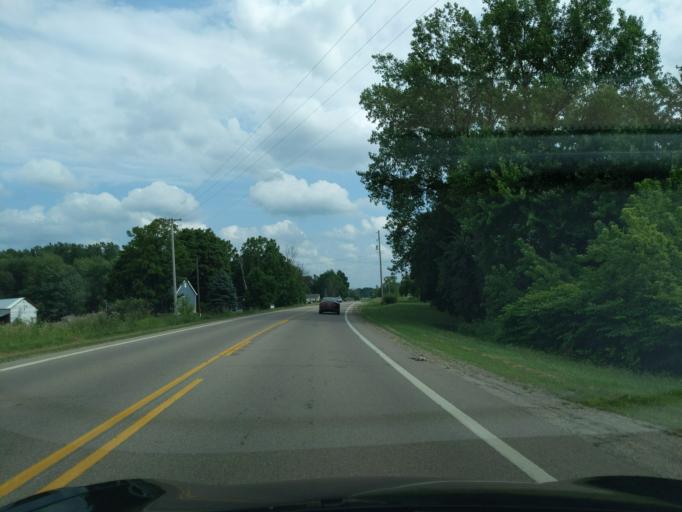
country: US
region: Michigan
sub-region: Eaton County
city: Eaton Rapids
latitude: 42.4577
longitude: -84.6547
